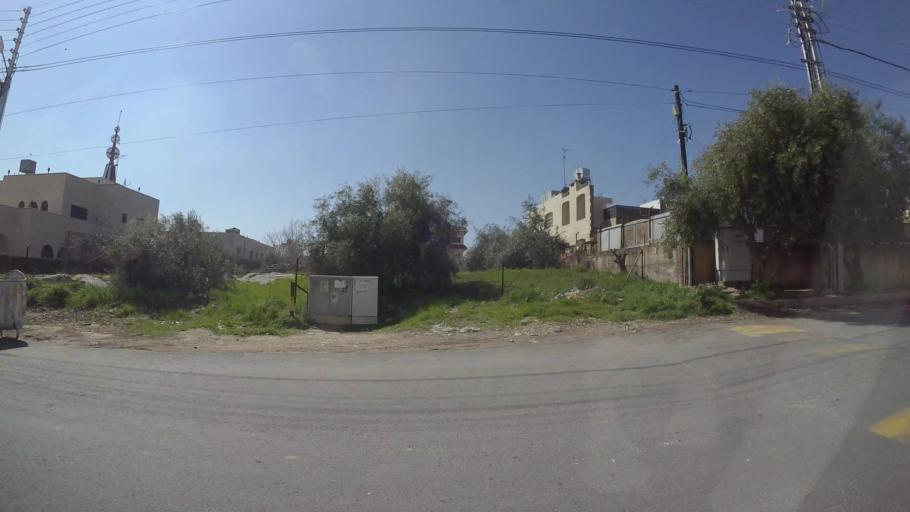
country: JO
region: Amman
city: Al Bunayyat ash Shamaliyah
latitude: 31.8979
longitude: 35.8858
